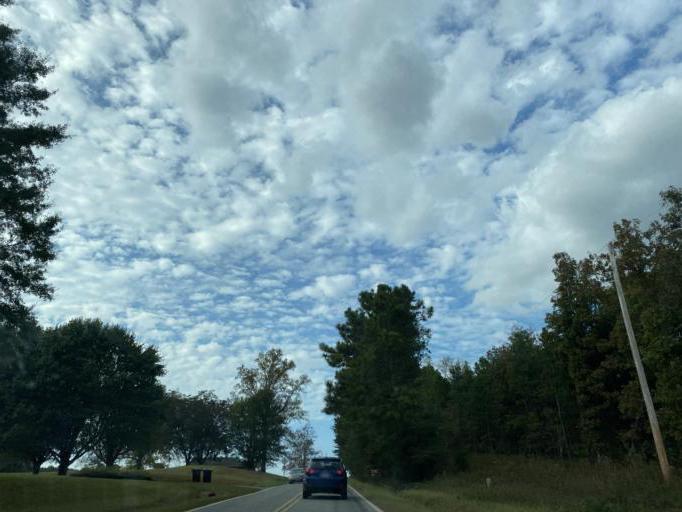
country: US
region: South Carolina
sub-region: Cherokee County
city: Gaffney
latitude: 35.0738
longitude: -81.7256
